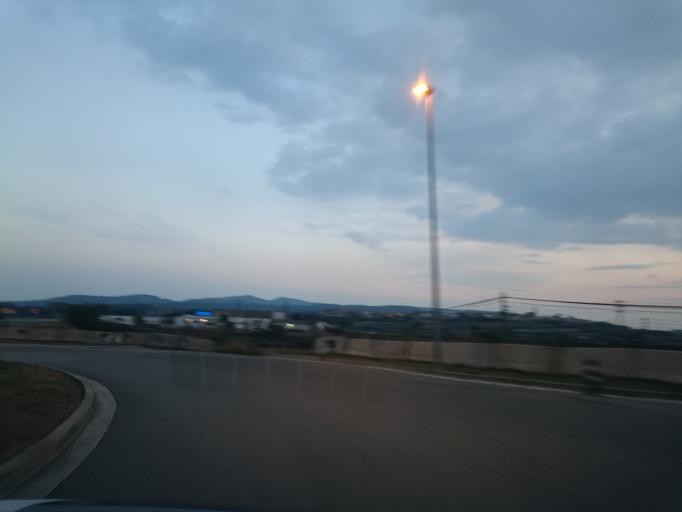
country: ES
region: Catalonia
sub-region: Provincia de Barcelona
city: Vilafranca del Penedes
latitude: 41.3351
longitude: 1.6969
